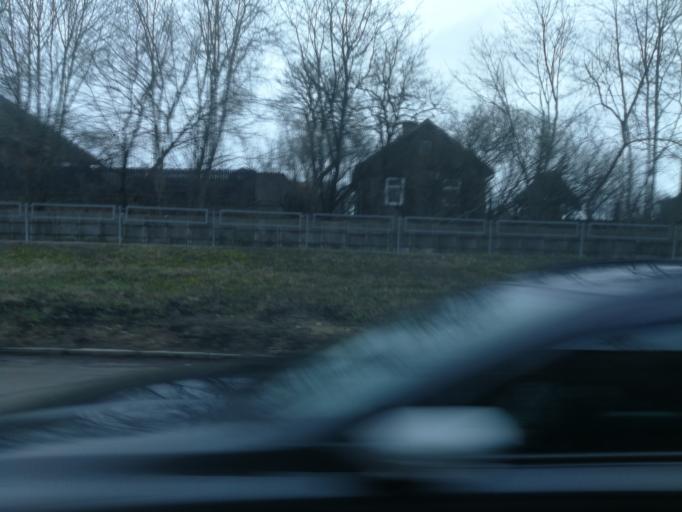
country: LV
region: Riga
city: Bolderaja
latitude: 57.0341
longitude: 24.1042
